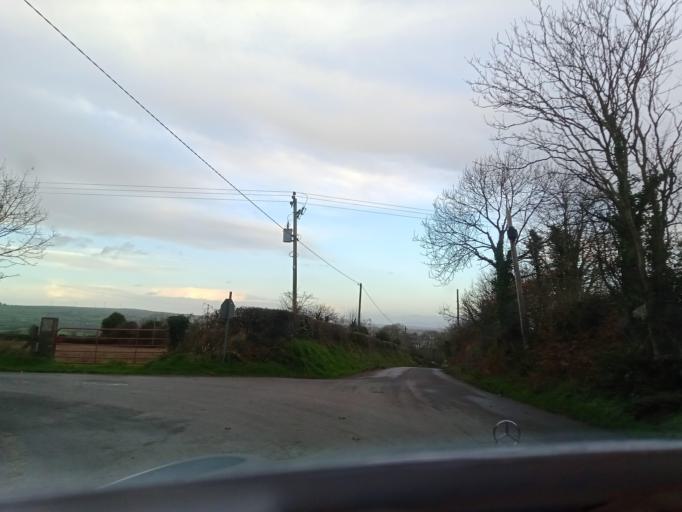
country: IE
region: Leinster
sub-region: Loch Garman
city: New Ross
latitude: 52.3422
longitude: -7.0325
